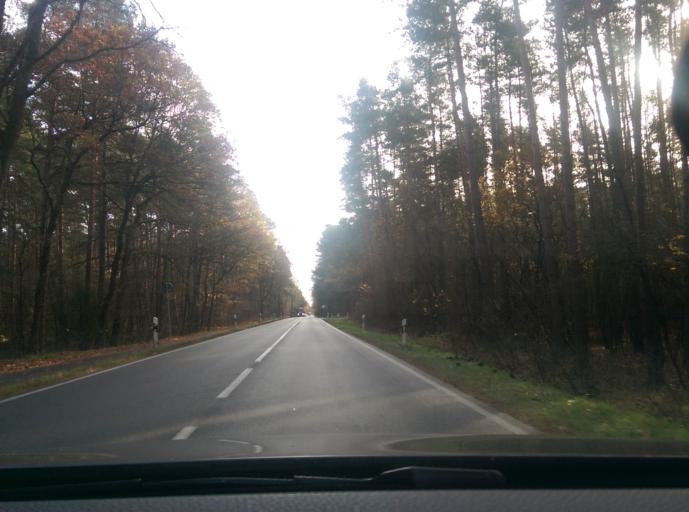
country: DE
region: Lower Saxony
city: Hambuhren
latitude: 52.6657
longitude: 9.9770
